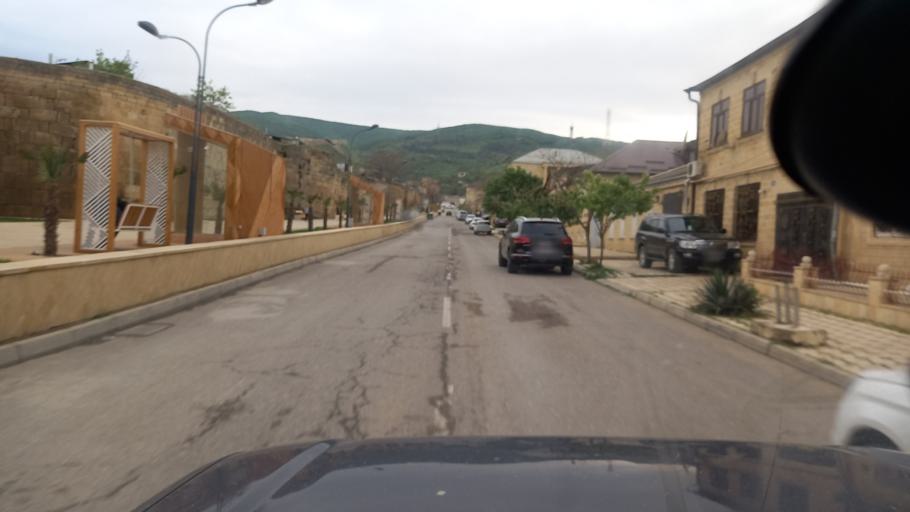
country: RU
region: Dagestan
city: Derbent
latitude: 42.0588
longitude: 48.2858
